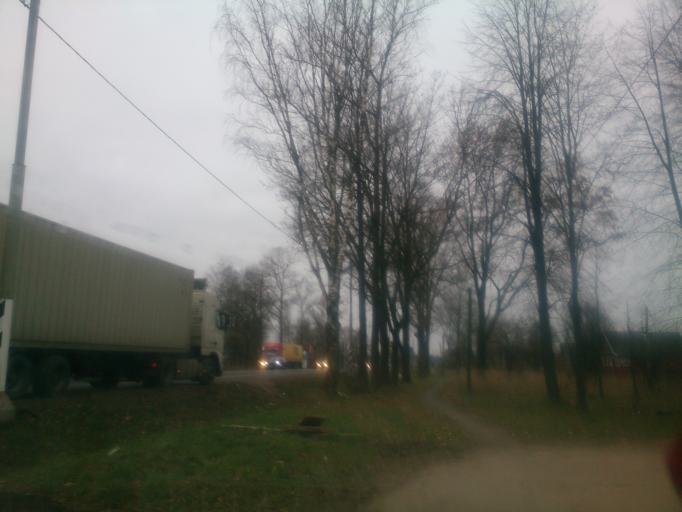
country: RU
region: Novgorod
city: Kresttsy
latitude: 58.3602
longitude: 32.2215
